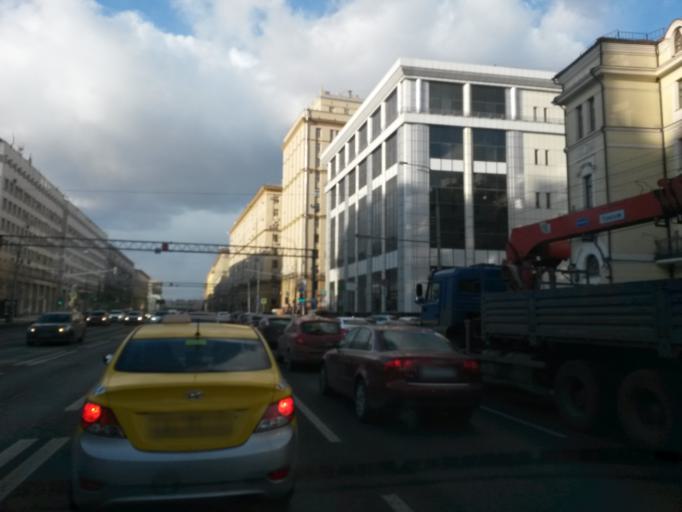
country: RU
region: Moscow
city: Mar'ina Roshcha
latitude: 55.7854
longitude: 37.6350
